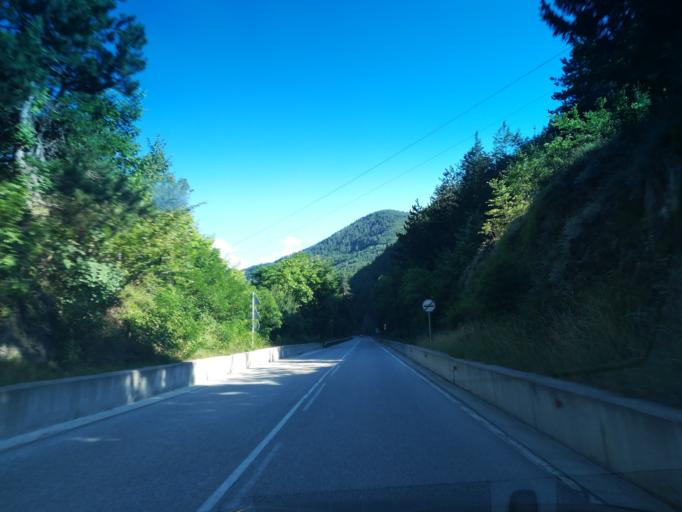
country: BG
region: Smolyan
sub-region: Obshtina Chepelare
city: Chepelare
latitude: 41.8352
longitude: 24.6834
